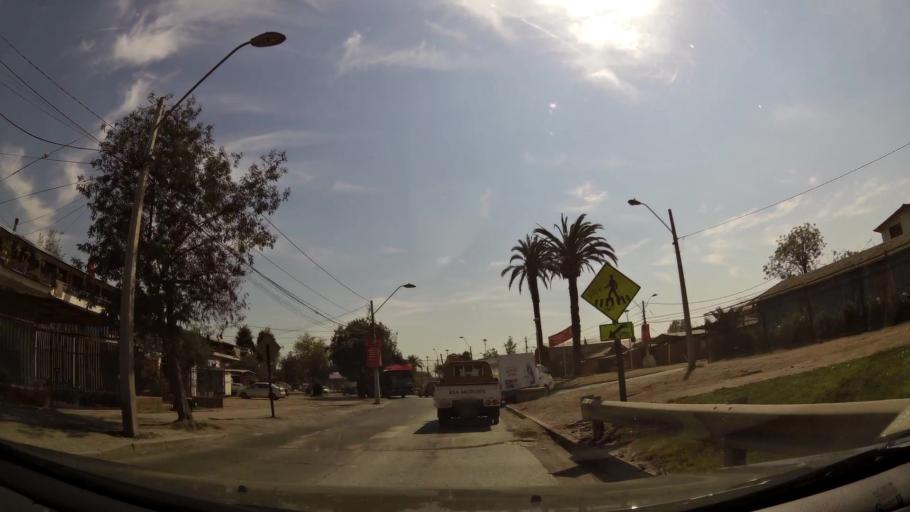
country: CL
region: Santiago Metropolitan
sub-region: Provincia de Santiago
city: La Pintana
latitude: -33.5665
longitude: -70.5981
